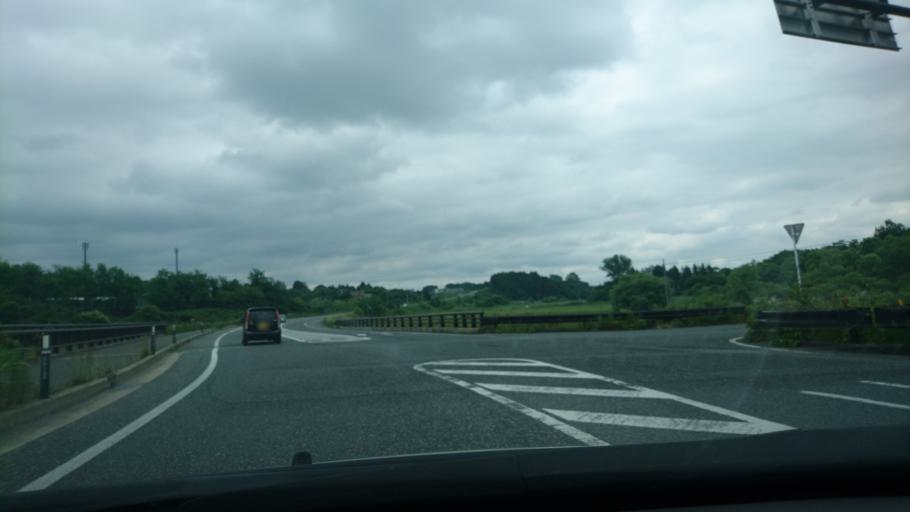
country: JP
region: Miyagi
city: Furukawa
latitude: 38.7213
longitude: 141.0248
